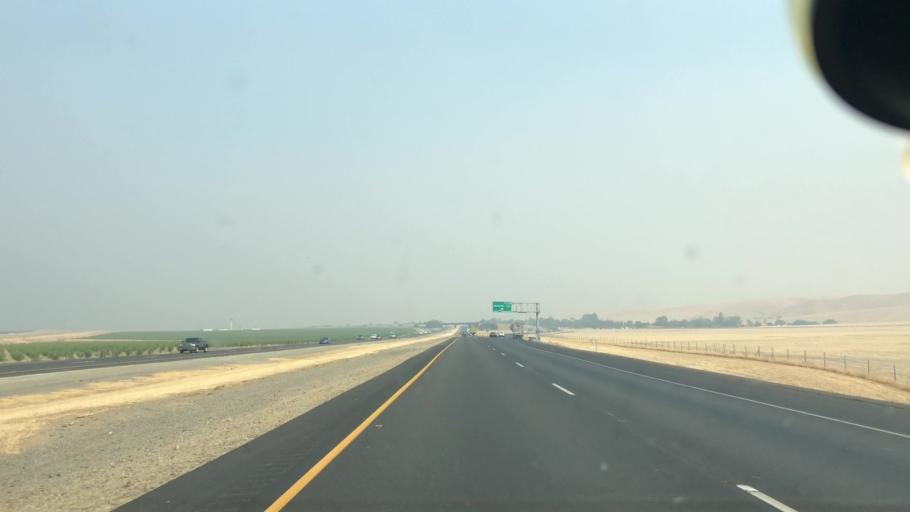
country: US
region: California
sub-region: San Joaquin County
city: Tracy
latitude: 37.6470
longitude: -121.4159
